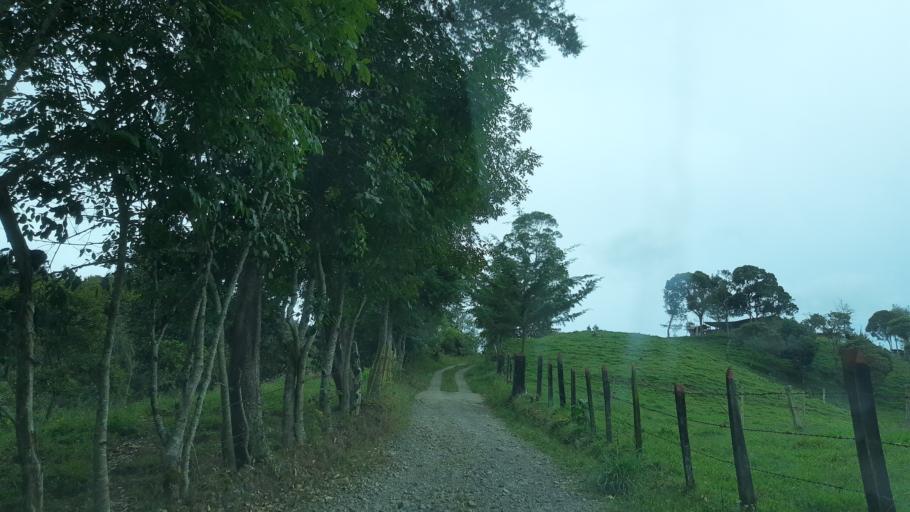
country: CO
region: Boyaca
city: Garagoa
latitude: 5.0829
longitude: -73.3515
